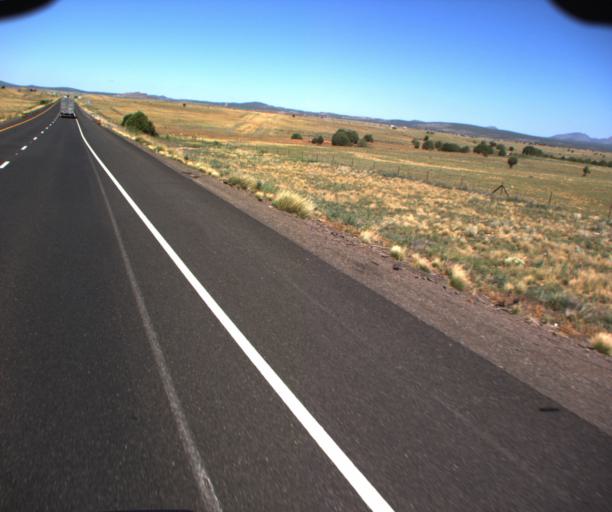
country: US
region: Arizona
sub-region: Yavapai County
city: Paulden
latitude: 35.2308
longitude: -112.5922
